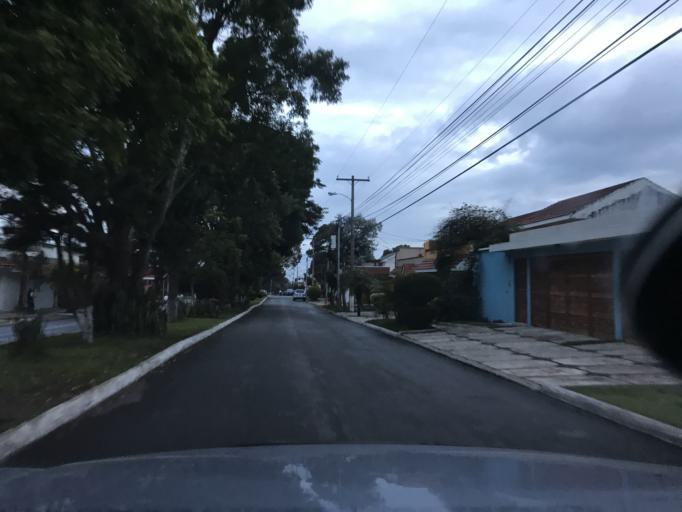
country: GT
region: Guatemala
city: Santa Catarina Pinula
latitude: 14.5825
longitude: -90.5511
